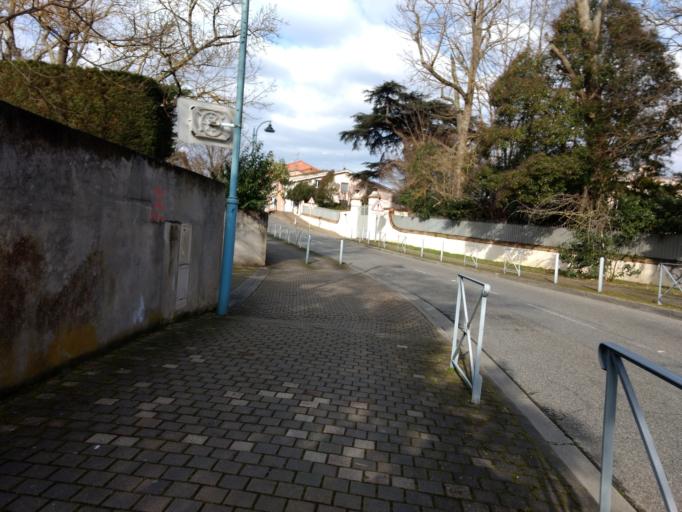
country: FR
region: Midi-Pyrenees
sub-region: Departement de la Haute-Garonne
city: Tournefeuille
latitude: 43.5828
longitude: 1.3491
